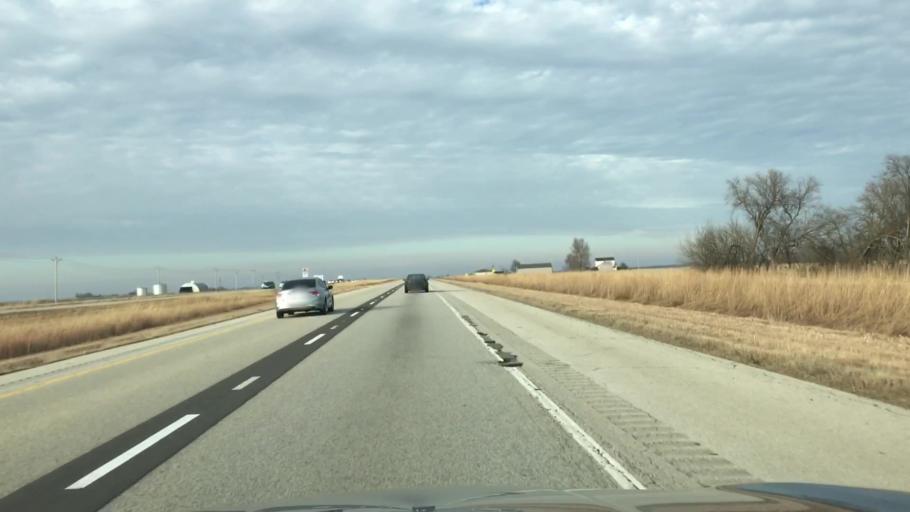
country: US
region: Illinois
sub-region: Sangamon County
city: Divernon
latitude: 39.4607
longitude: -89.6441
